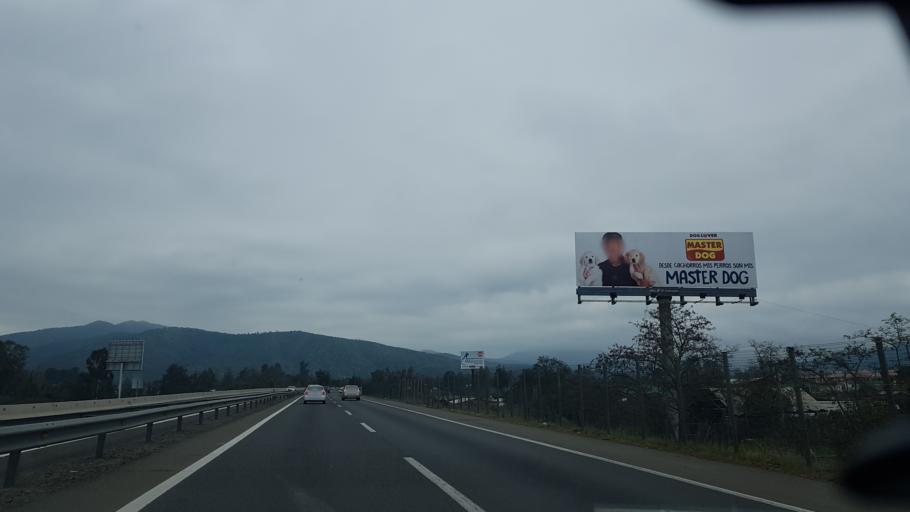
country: CL
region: Santiago Metropolitan
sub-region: Provincia de Melipilla
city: Melipilla
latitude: -33.4126
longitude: -71.1493
